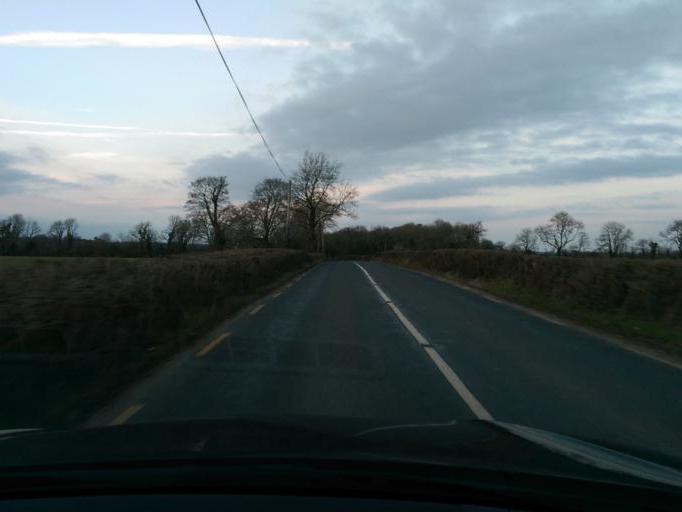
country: IE
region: Connaught
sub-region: County Galway
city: Portumna
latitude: 53.0371
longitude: -8.1153
